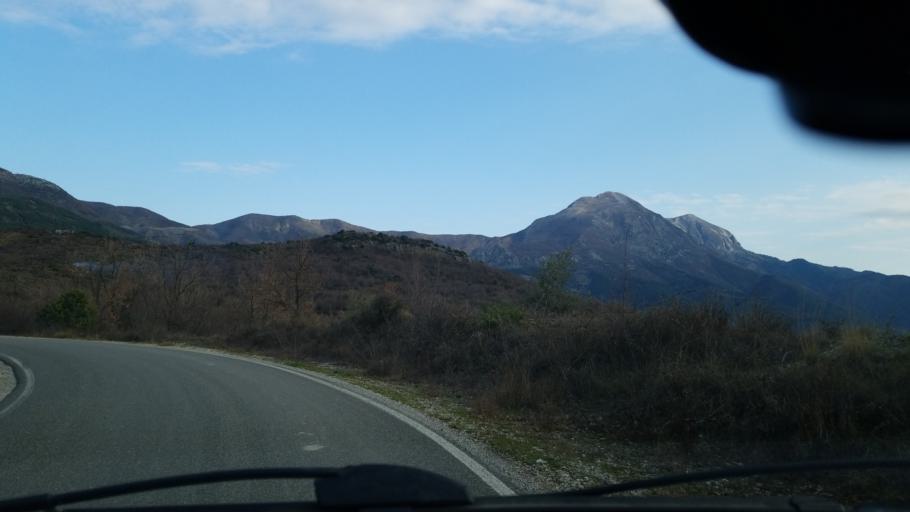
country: AL
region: Lezhe
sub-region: Rrethi i Lezhes
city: Kallmeti i Madh
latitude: 41.8787
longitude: 19.6928
